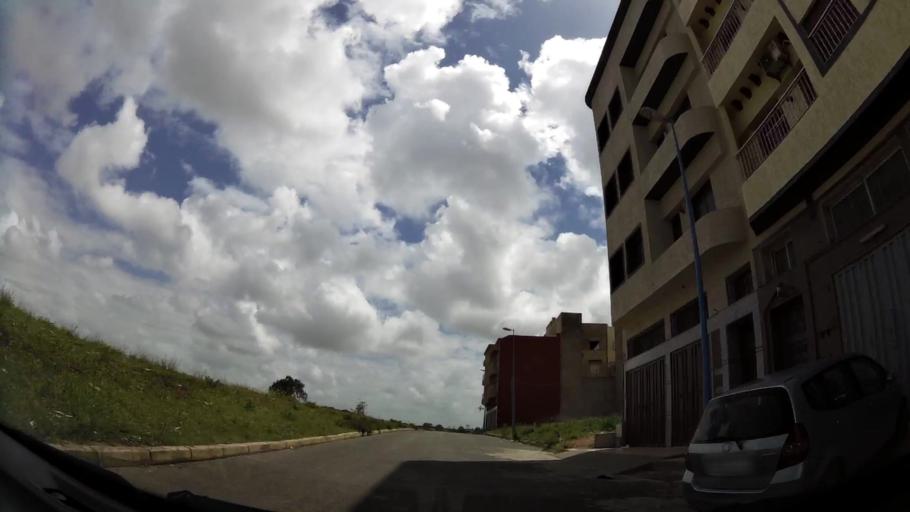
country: MA
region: Grand Casablanca
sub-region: Casablanca
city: Casablanca
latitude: 33.5243
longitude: -7.6003
